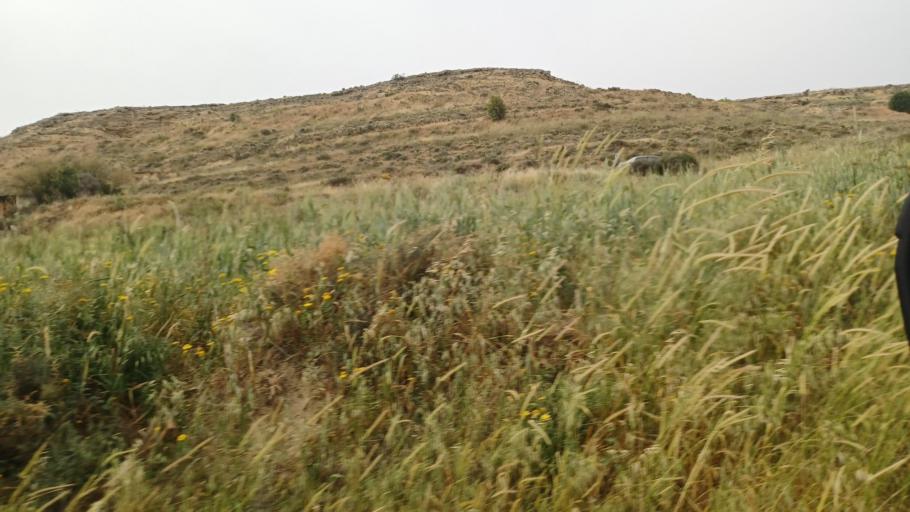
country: CY
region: Lefkosia
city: Mammari
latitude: 35.1812
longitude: 33.1762
